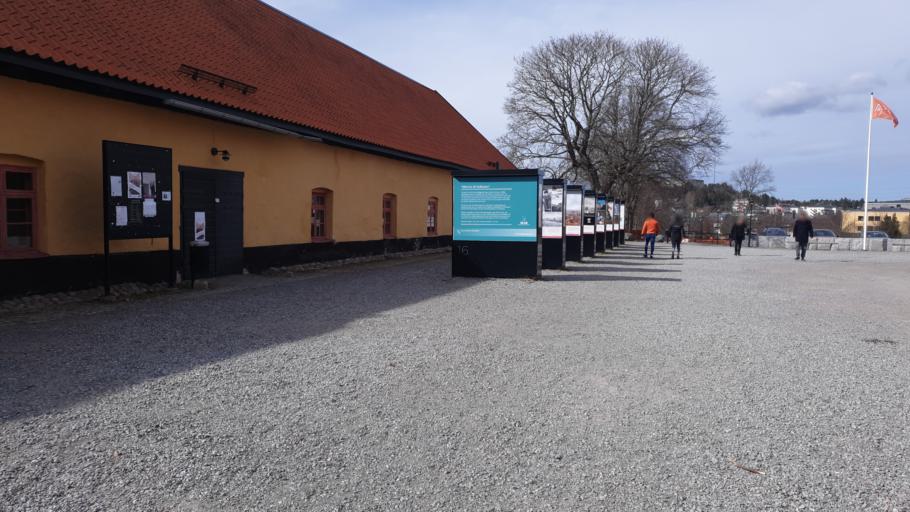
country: SE
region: Stockholm
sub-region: Sollentuna Kommun
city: Sollentuna
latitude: 59.4402
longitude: 17.9583
